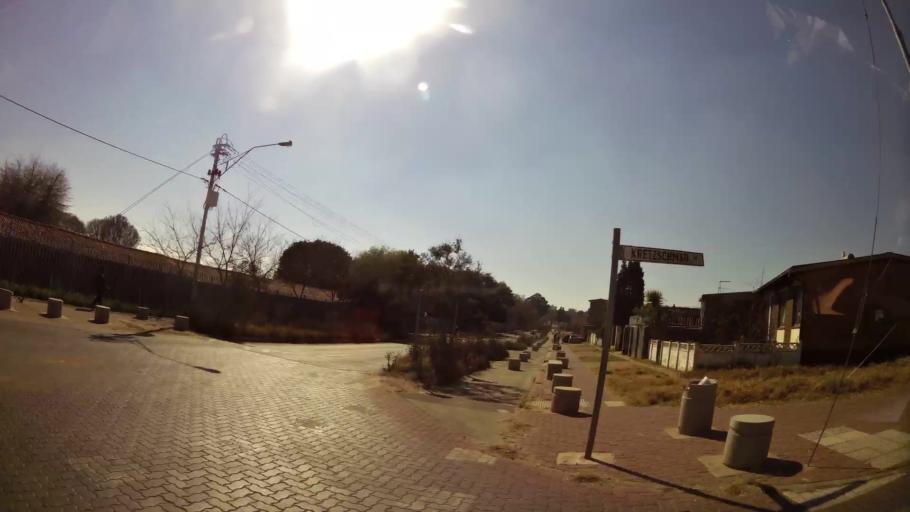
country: ZA
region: Gauteng
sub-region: City of Johannesburg Metropolitan Municipality
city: Johannesburg
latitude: -26.1820
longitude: 27.9705
